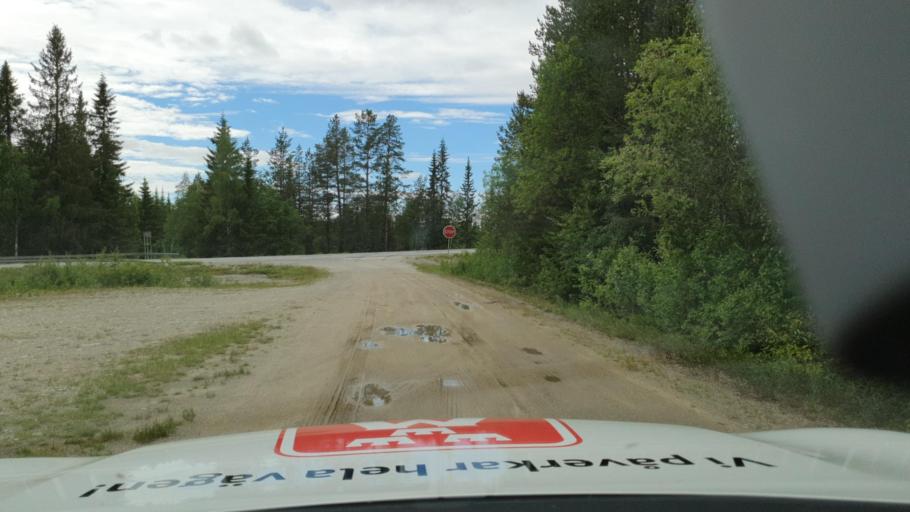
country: SE
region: Vaesterbotten
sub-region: Asele Kommun
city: Insjon
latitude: 64.3526
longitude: 17.9001
